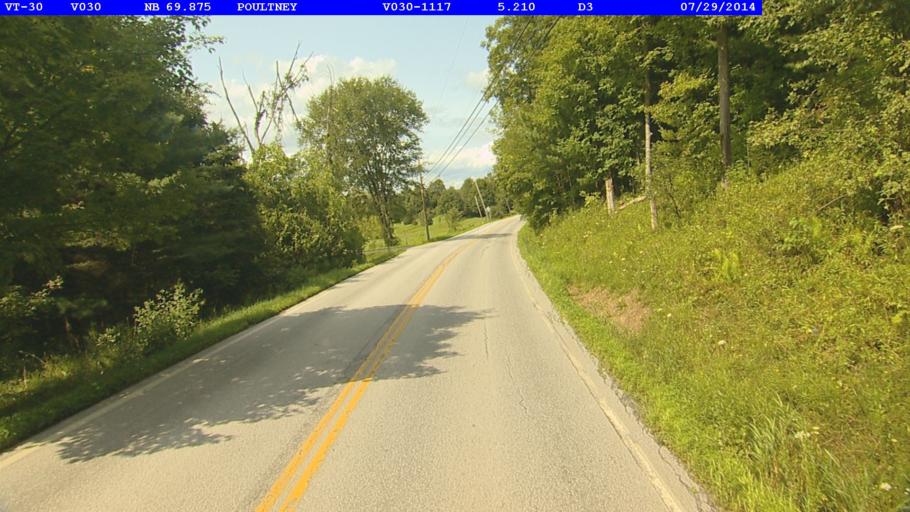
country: US
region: Vermont
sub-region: Rutland County
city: Poultney
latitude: 43.5262
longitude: -73.2313
